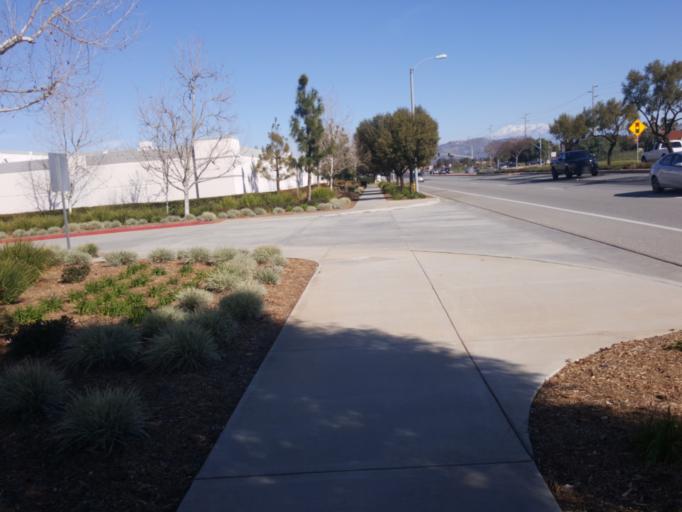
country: US
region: California
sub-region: Riverside County
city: March Air Force Base
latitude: 33.9104
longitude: -117.2549
